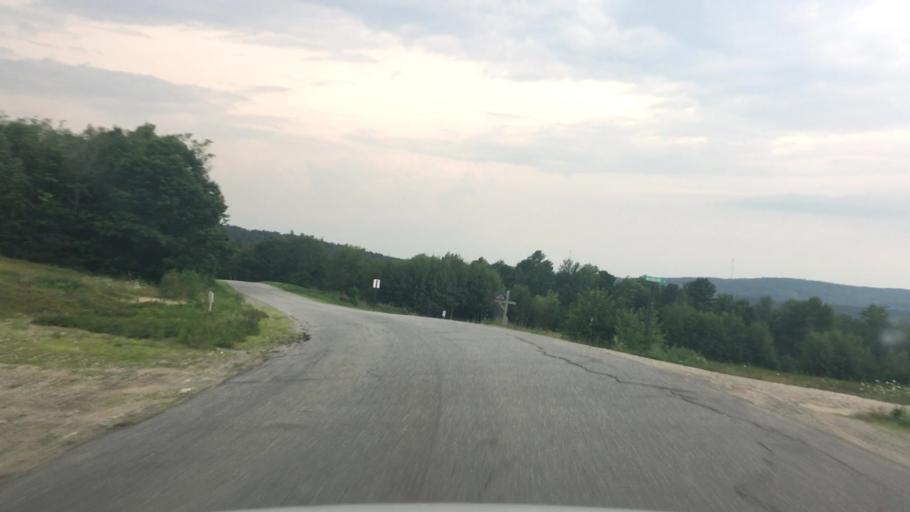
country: US
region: Maine
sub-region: Knox County
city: Washington
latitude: 44.3685
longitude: -69.3422
